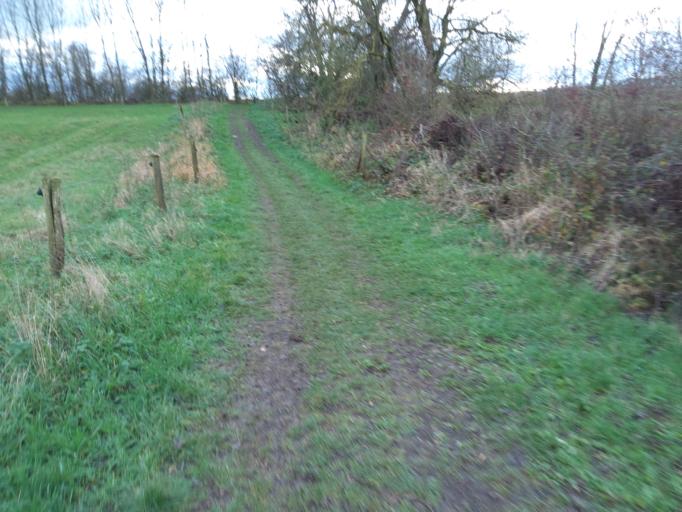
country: NL
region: Gelderland
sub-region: Gemeente Neerijnen
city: Neerijnen
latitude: 51.8228
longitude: 5.2689
